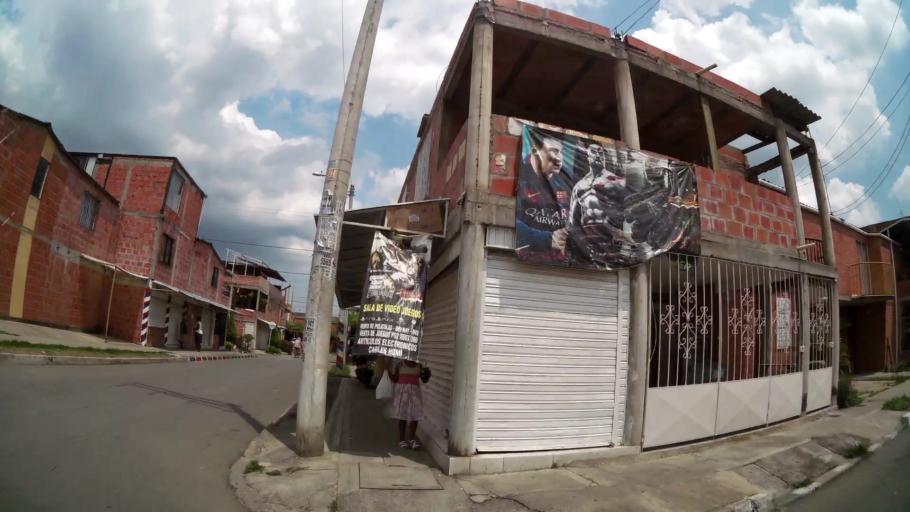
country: CO
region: Valle del Cauca
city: Cali
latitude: 3.4597
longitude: -76.4635
